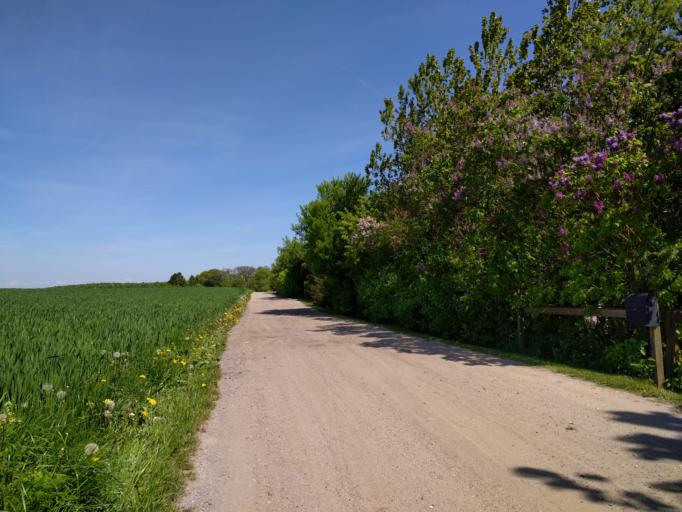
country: DK
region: Zealand
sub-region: Guldborgsund Kommune
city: Stubbekobing
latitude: 54.7523
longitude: 12.0357
